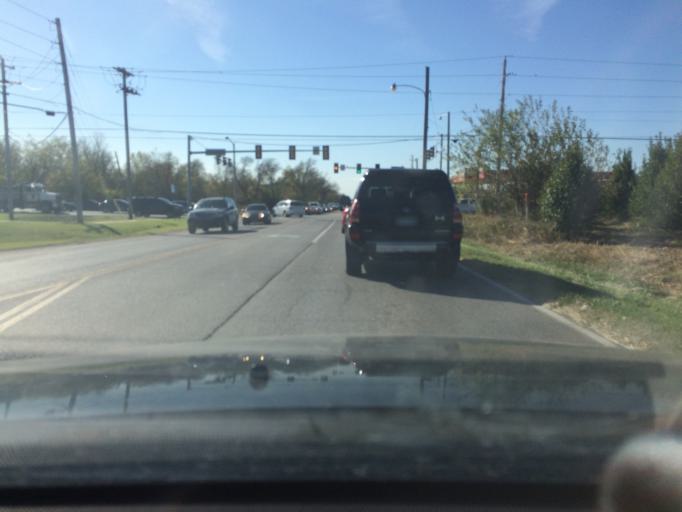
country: US
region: Oklahoma
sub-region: Tulsa County
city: Broken Arrow
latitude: 36.0900
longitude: -95.8145
